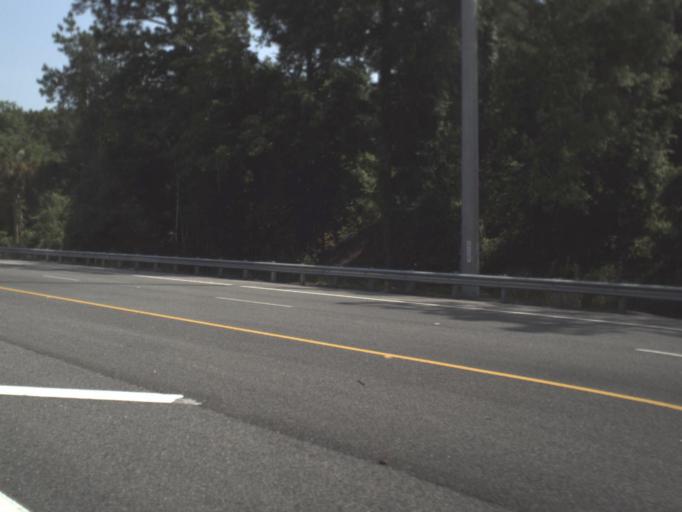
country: US
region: Florida
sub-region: Saint Johns County
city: Palm Valley
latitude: 30.1005
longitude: -81.4747
